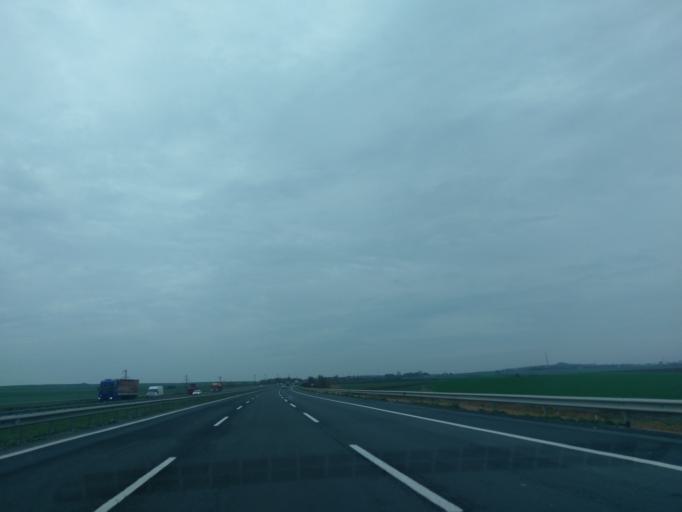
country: TR
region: Istanbul
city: Canta
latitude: 41.1281
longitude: 28.1617
